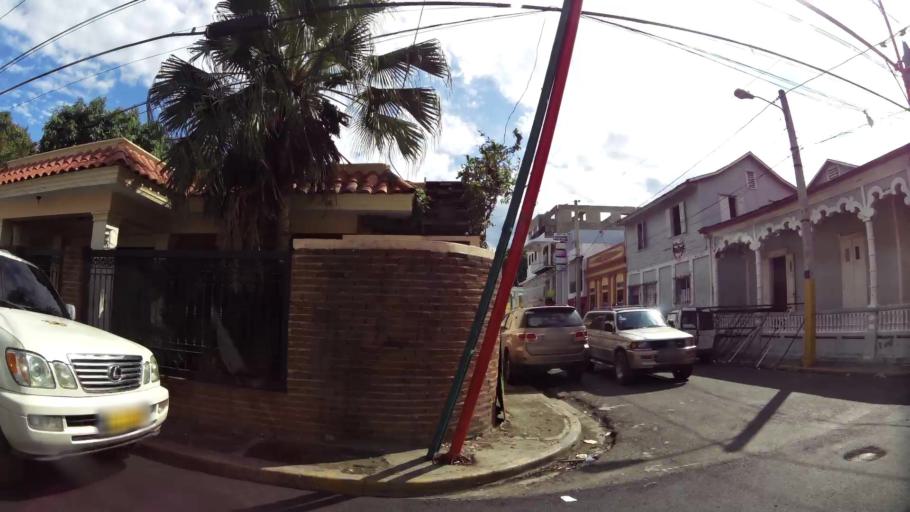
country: DO
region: La Vega
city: Concepcion de La Vega
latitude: 19.2235
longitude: -70.5287
